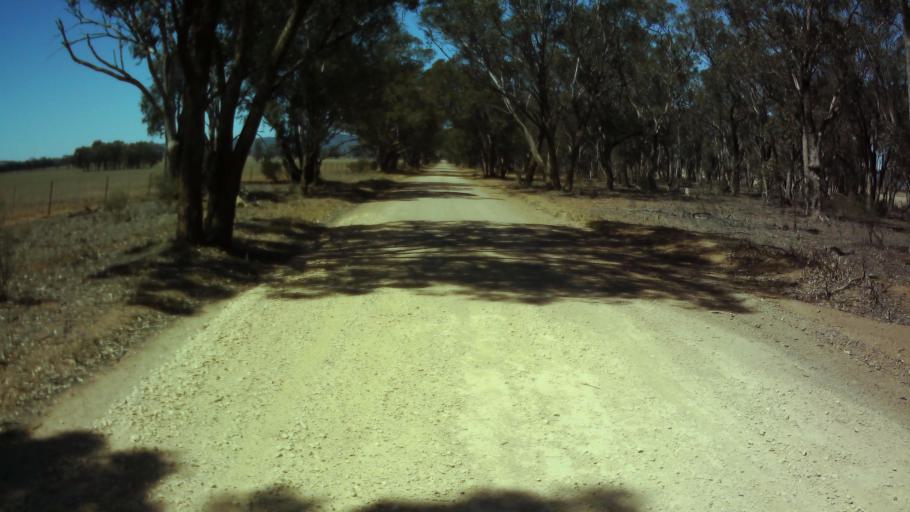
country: AU
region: New South Wales
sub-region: Weddin
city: Grenfell
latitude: -33.8950
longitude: 148.0850
